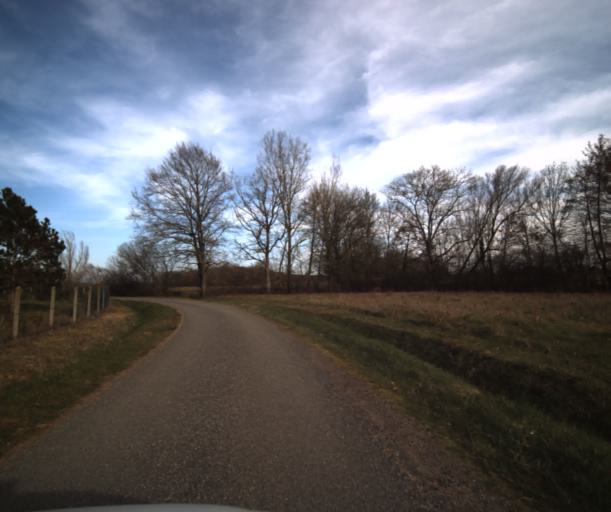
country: FR
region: Midi-Pyrenees
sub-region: Departement du Tarn-et-Garonne
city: Labastide-Saint-Pierre
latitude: 43.9070
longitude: 1.3717
